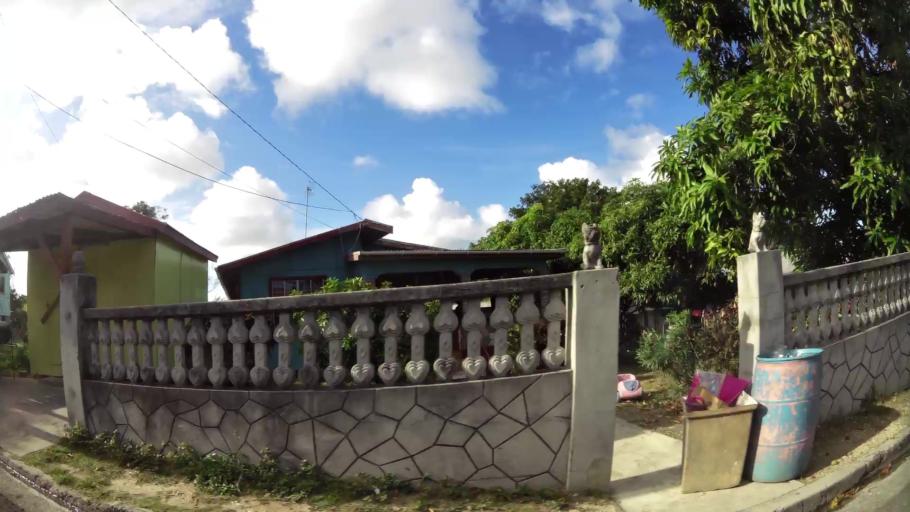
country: AG
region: Saint Peter
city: All Saints
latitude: 17.0666
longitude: -61.7942
